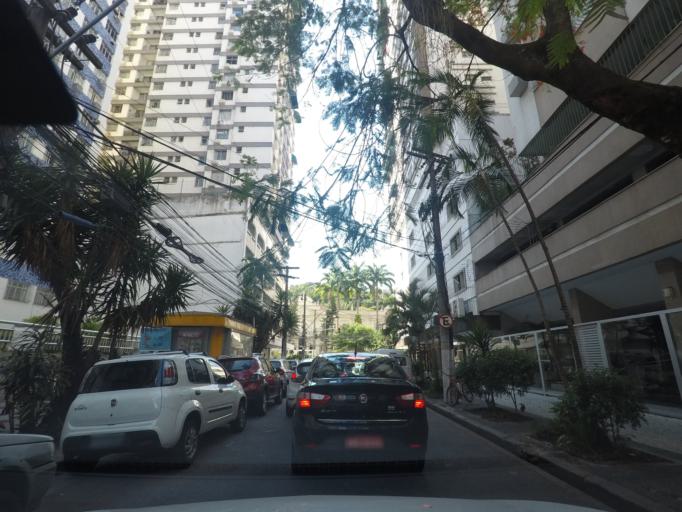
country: BR
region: Rio de Janeiro
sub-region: Niteroi
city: Niteroi
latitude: -22.9023
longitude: -43.1137
